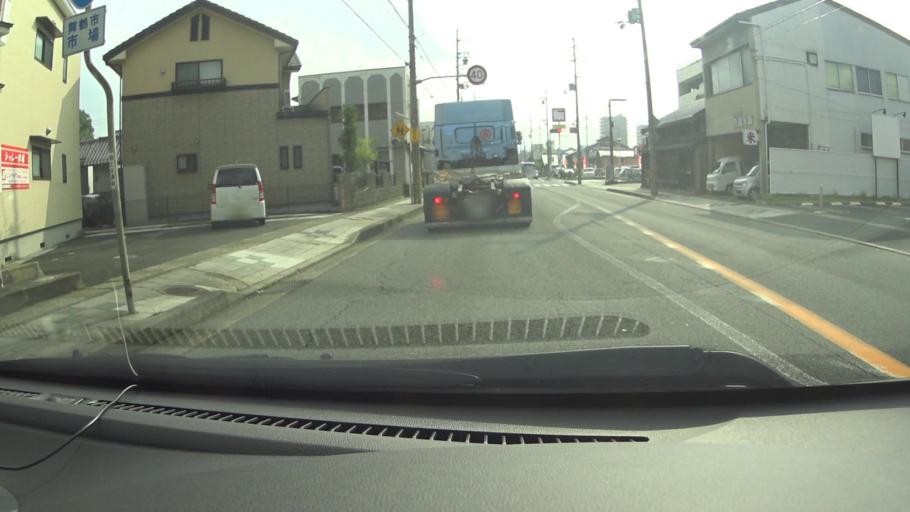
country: JP
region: Kyoto
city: Maizuru
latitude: 35.4772
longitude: 135.4045
